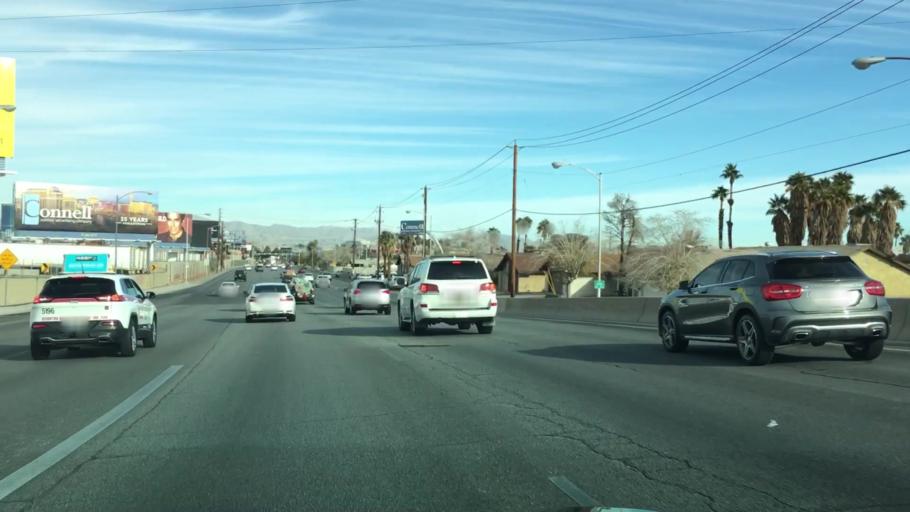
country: US
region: Nevada
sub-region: Clark County
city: Paradise
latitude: 36.0934
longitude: -115.1460
